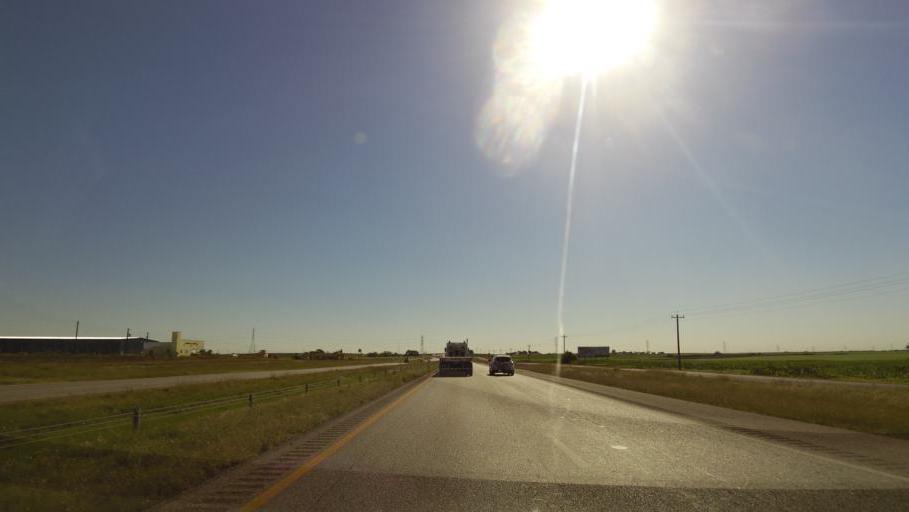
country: US
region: Texas
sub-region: Guadalupe County
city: Marion
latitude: 29.5335
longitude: -98.0952
